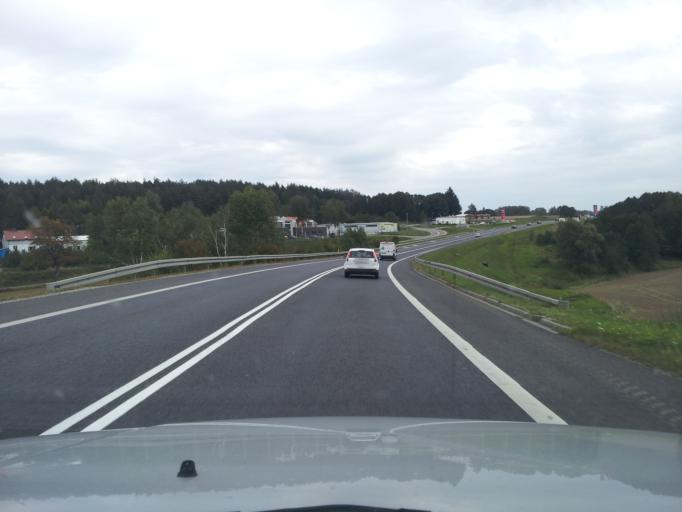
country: PL
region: Warmian-Masurian Voivodeship
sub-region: Powiat olsztynski
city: Gietrzwald
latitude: 53.7479
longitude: 20.2458
